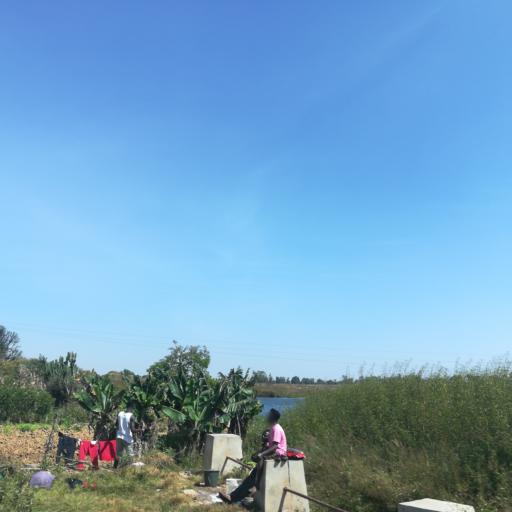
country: NG
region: Plateau
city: Bukuru
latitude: 9.7587
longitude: 8.8644
